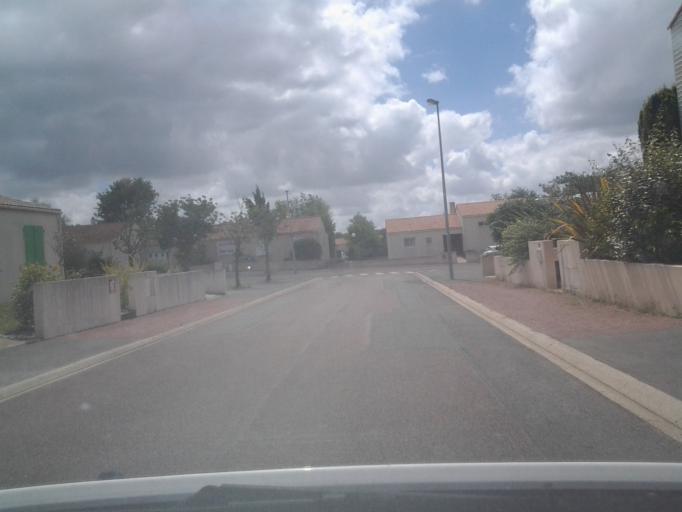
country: FR
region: Pays de la Loire
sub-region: Departement de la Vendee
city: La Roche-sur-Yon
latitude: 46.6560
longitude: -1.4536
